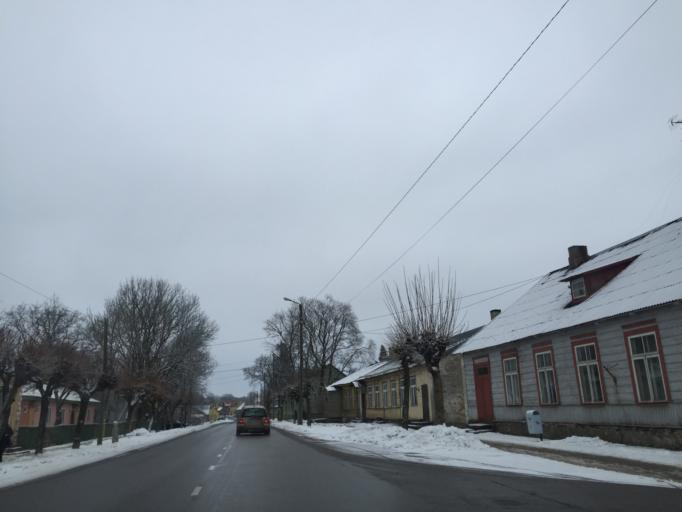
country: EE
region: Laeaene
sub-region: Lihula vald
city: Lihula
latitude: 58.6846
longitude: 23.8307
